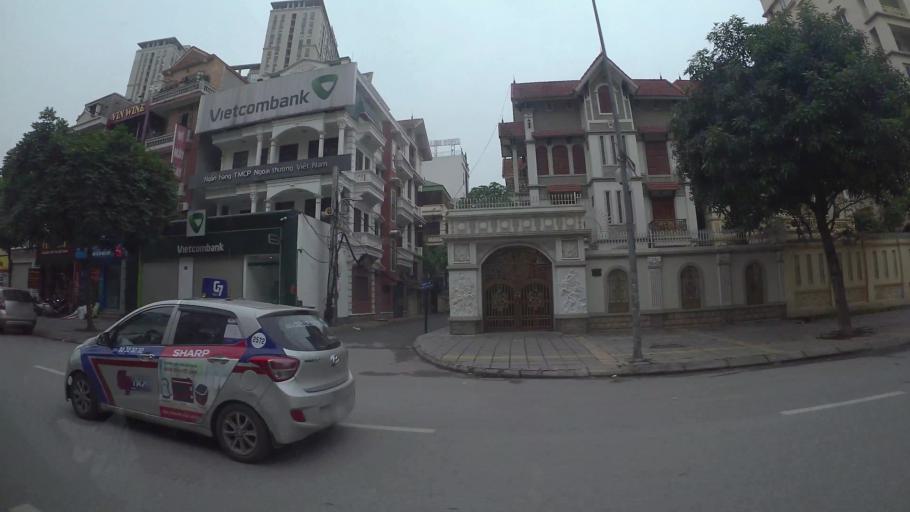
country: VN
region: Ha Noi
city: Cau Giay
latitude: 21.0178
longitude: 105.7933
